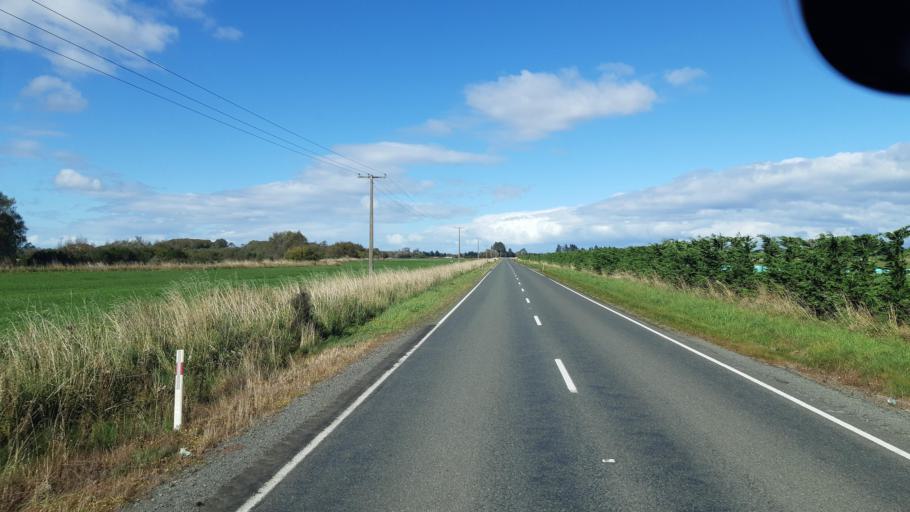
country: NZ
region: Southland
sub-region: Southland District
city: Winton
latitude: -45.9381
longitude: 168.1141
